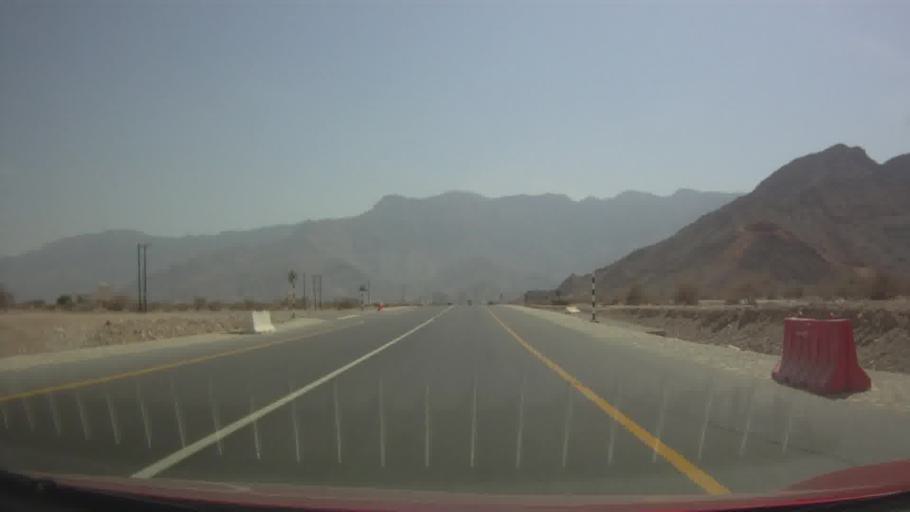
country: OM
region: Muhafazat Masqat
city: Muscat
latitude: 23.4213
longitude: 58.7814
